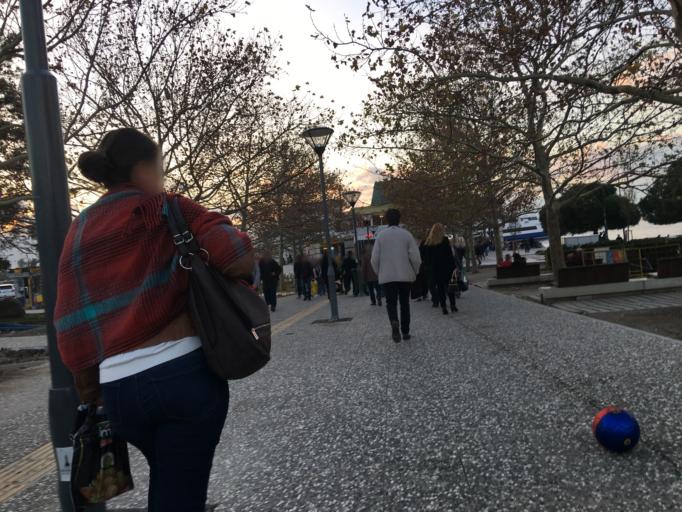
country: TR
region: Izmir
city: Izmir
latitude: 38.4186
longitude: 27.1270
